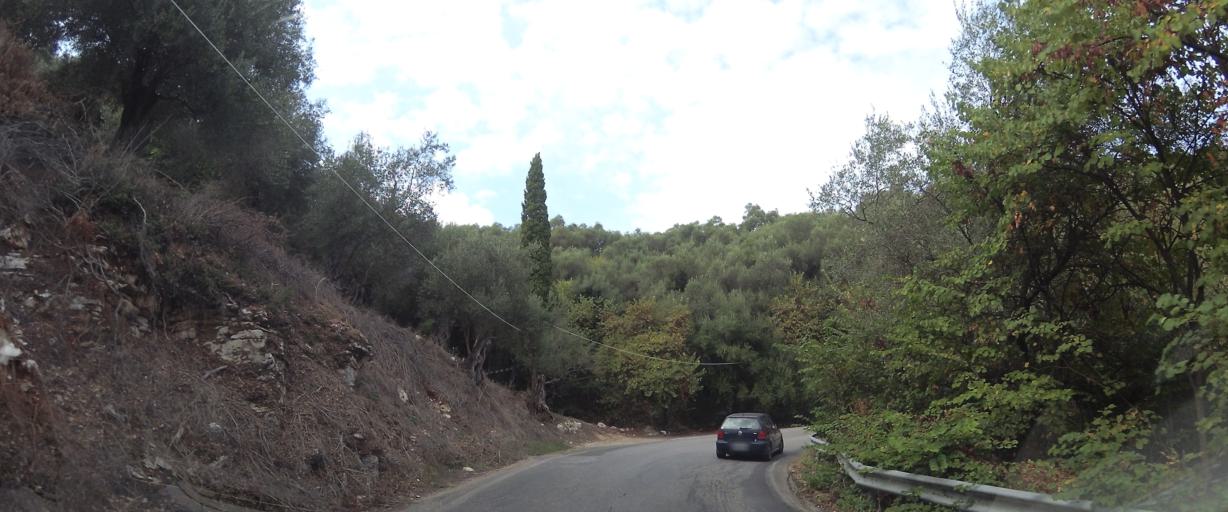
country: GR
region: Ionian Islands
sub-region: Nomos Kerkyras
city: Acharavi
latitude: 39.7575
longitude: 19.9325
